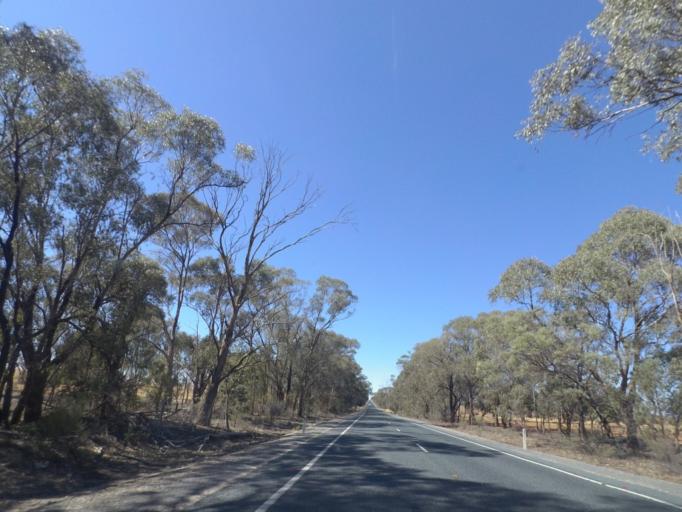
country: AU
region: New South Wales
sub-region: Bland
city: West Wyalong
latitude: -34.1478
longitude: 147.1190
